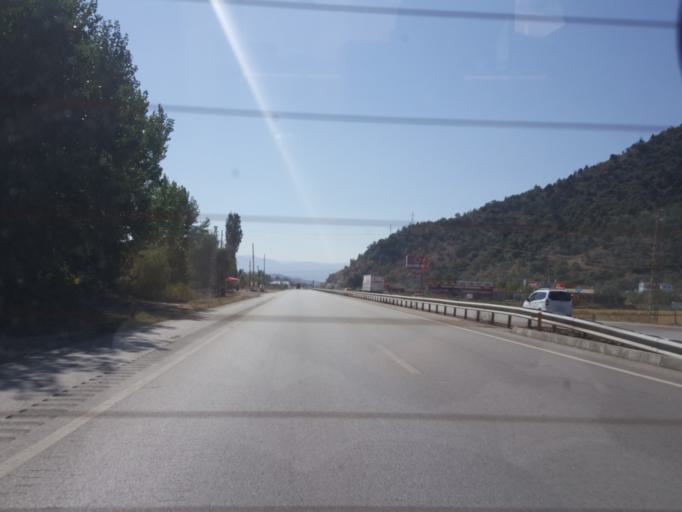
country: TR
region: Corum
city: Osmancik
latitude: 40.9740
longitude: 34.9125
